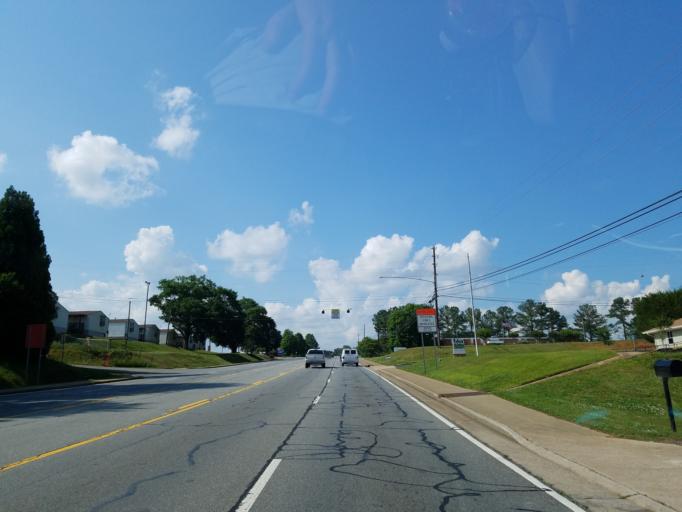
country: US
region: Georgia
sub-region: Cherokee County
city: Canton
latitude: 34.2310
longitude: -84.5000
